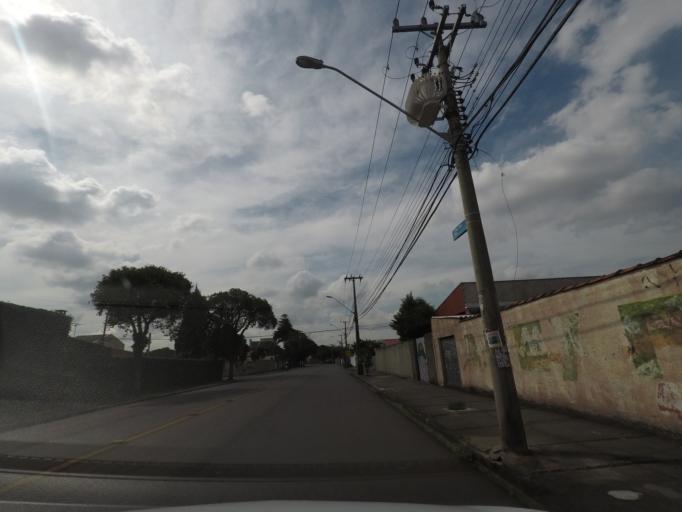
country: BR
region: Parana
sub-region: Pinhais
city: Pinhais
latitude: -25.4744
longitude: -49.2009
